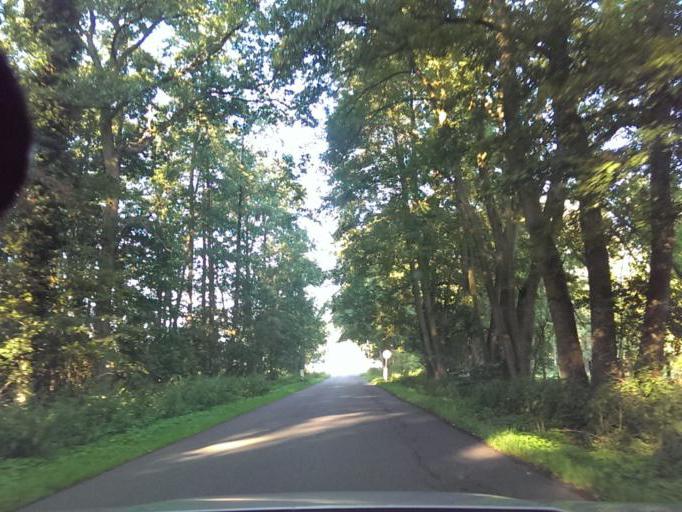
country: DE
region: Lower Saxony
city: Elze
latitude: 52.5644
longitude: 9.7418
